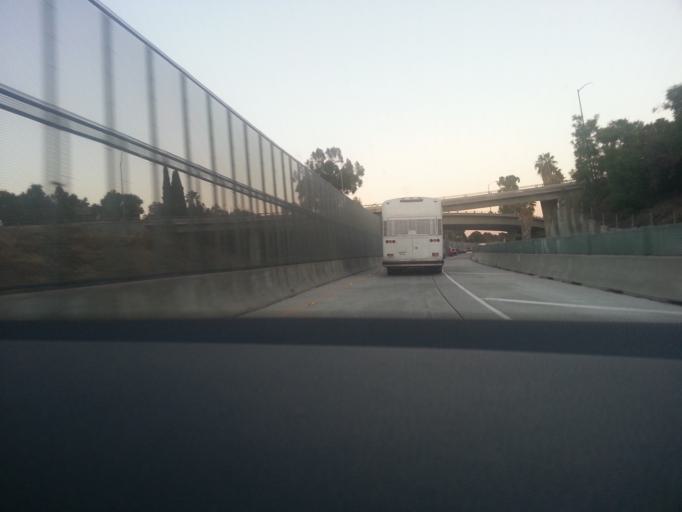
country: US
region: California
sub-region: Los Angeles County
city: Boyle Heights
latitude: 34.0556
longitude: -118.2019
